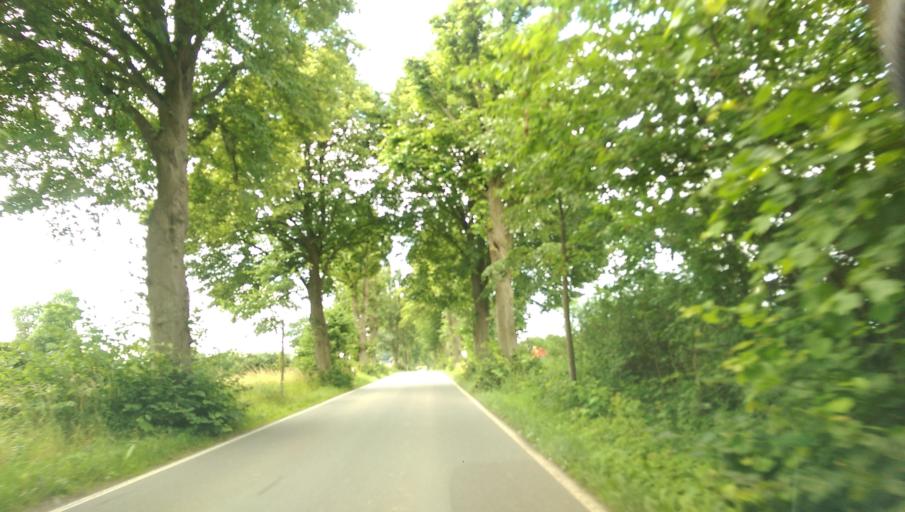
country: DE
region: Schleswig-Holstein
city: Travemuende
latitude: 53.9747
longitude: 10.8276
